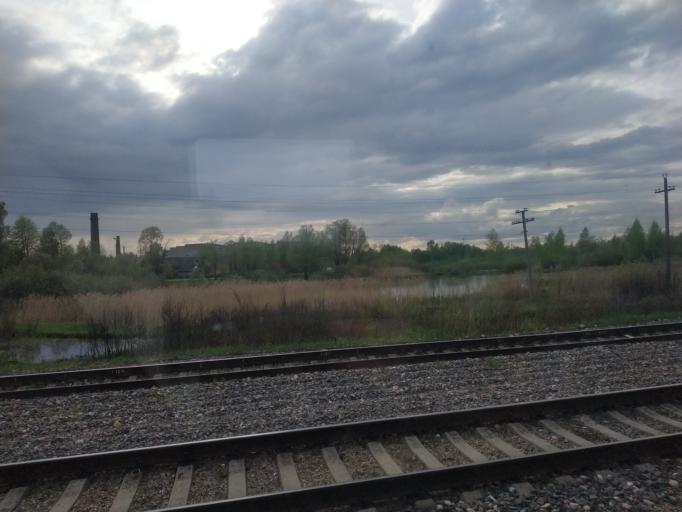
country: RU
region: Smolensk
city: Ugra
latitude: 54.7735
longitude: 34.3427
